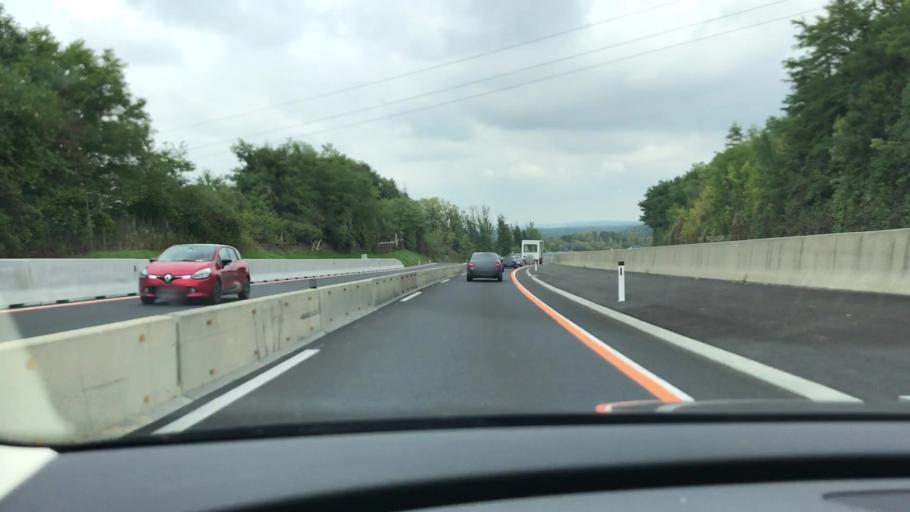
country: AT
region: Styria
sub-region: Politischer Bezirk Leibnitz
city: Spielfeld
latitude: 46.7019
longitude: 15.6380
